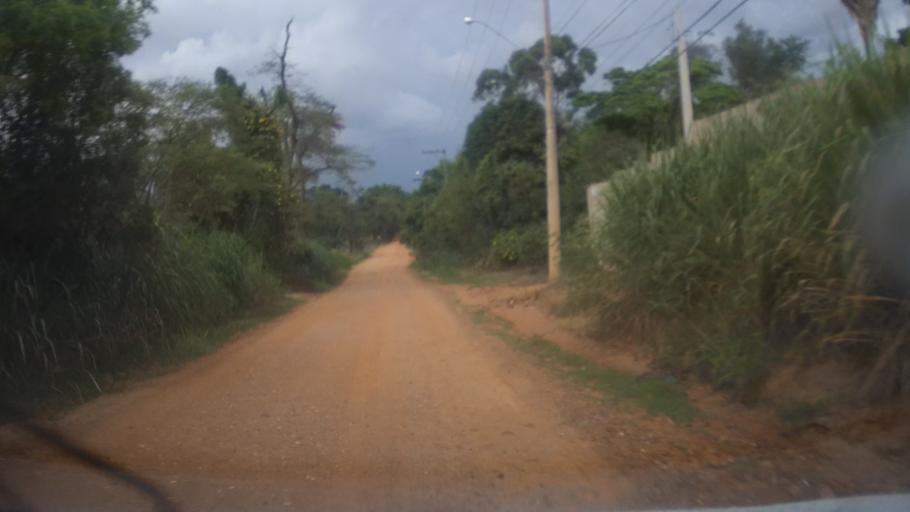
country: BR
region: Sao Paulo
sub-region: Itupeva
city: Itupeva
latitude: -23.1939
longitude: -47.0092
